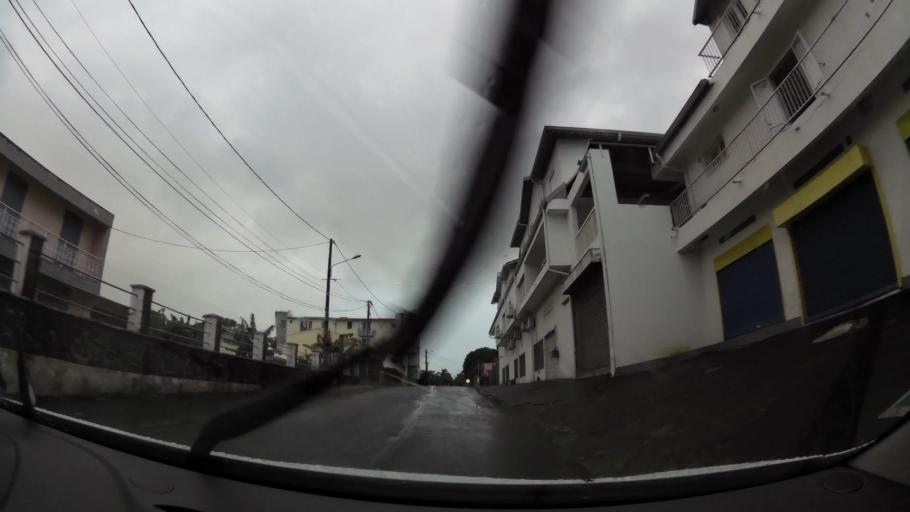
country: RE
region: Reunion
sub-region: Reunion
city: Saint-Benoit
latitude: -21.0384
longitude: 55.7138
